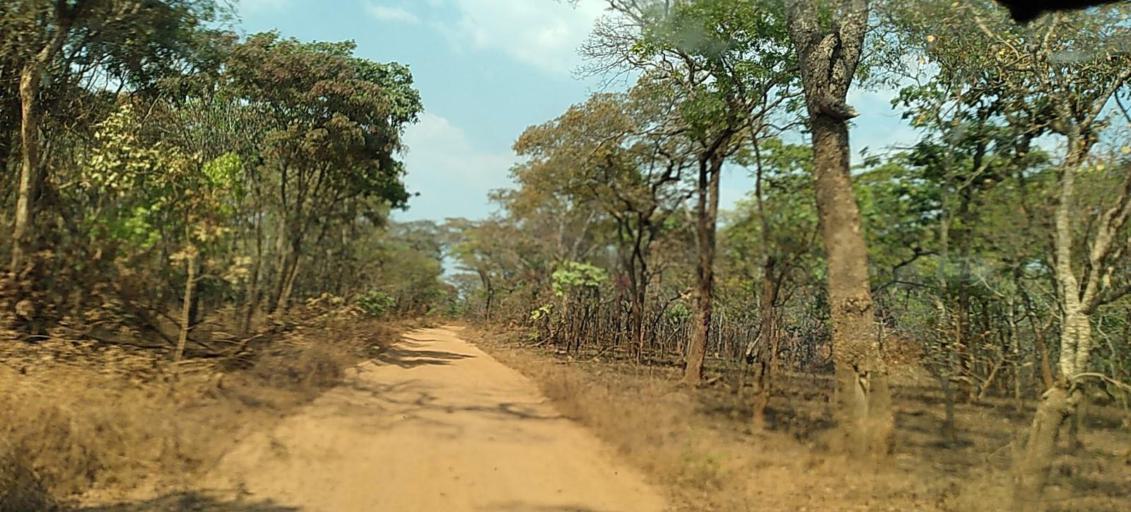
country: ZM
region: North-Western
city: Kasempa
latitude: -13.3199
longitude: 26.0477
